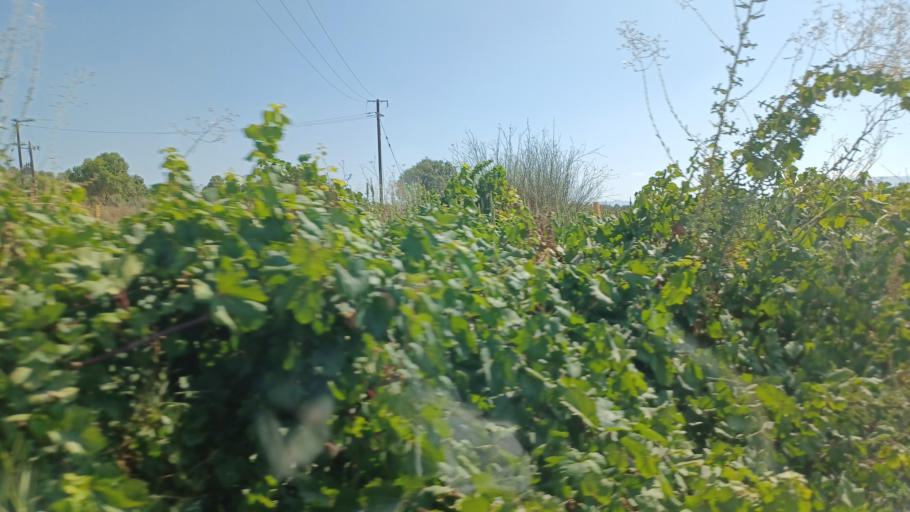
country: CY
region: Pafos
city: Tala
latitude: 34.8902
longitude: 32.4992
